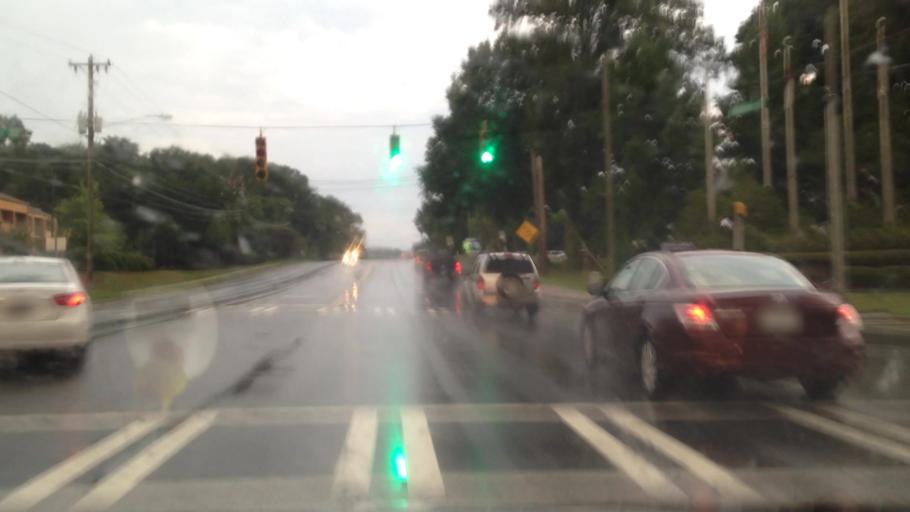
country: US
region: North Carolina
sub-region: Mecklenburg County
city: Pineville
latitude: 35.1360
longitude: -80.9037
